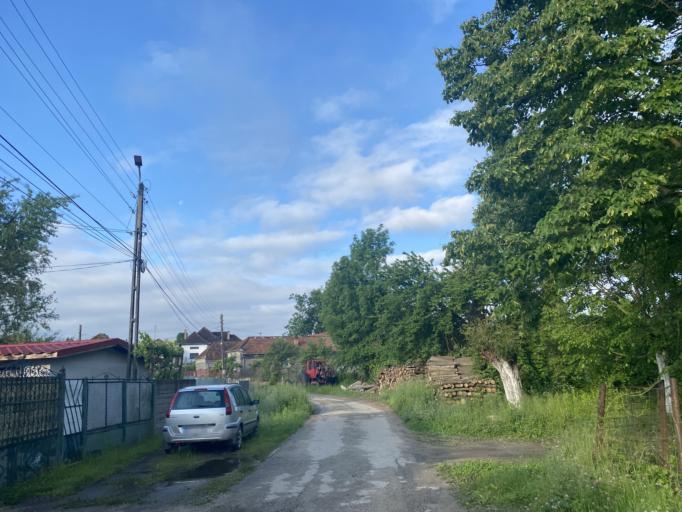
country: RO
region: Hunedoara
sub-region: Comuna Bosorod
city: Bosorod
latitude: 45.7032
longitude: 23.0654
